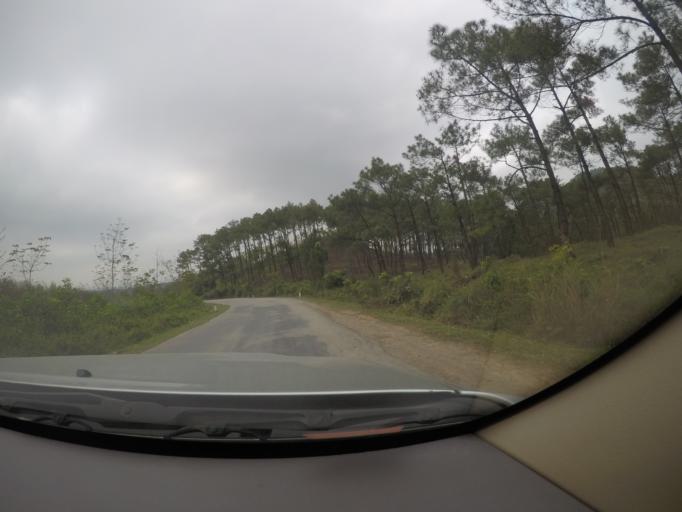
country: VN
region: Quang Binh
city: Ba Don
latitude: 17.6524
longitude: 106.4352
